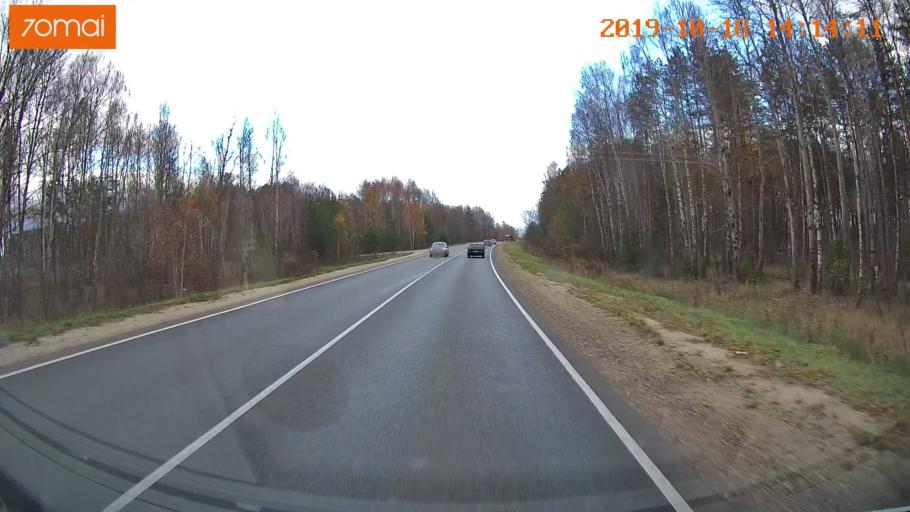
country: RU
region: Rjazan
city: Spas-Klepiki
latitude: 55.1521
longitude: 40.2890
